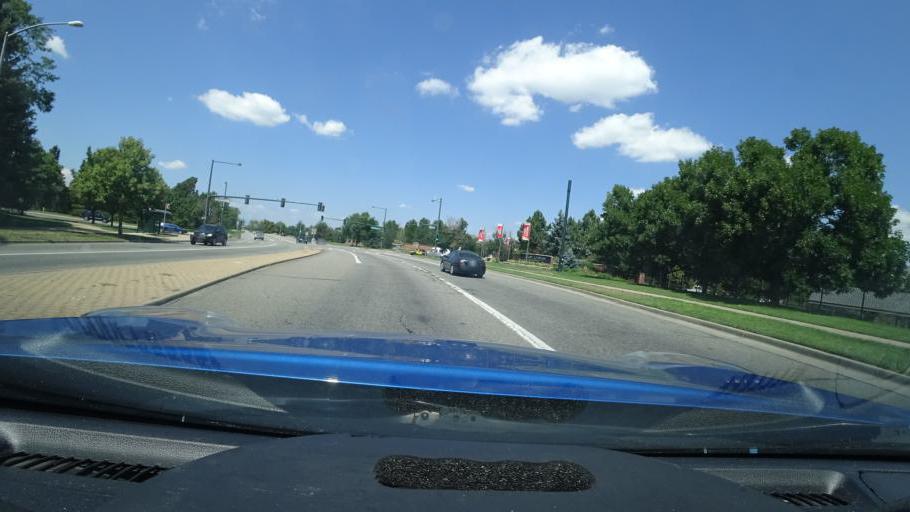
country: US
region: Colorado
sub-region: Arapahoe County
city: Glendale
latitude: 39.7110
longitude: -104.8919
